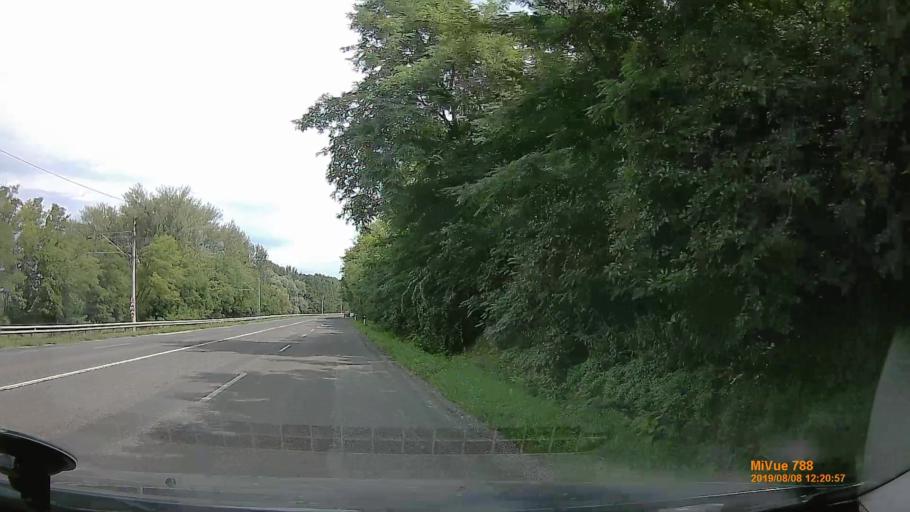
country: HU
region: Somogy
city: Zamardi
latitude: 46.8747
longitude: 17.9277
